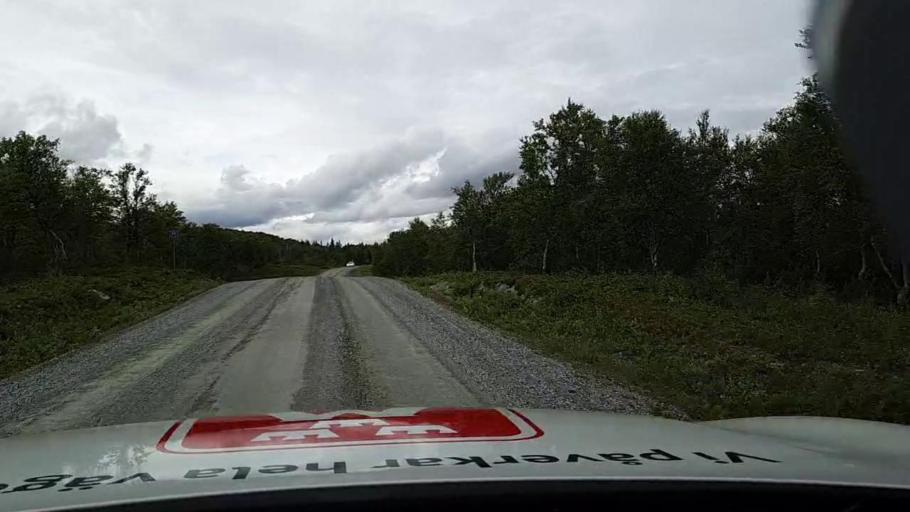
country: SE
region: Jaemtland
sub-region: Are Kommun
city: Are
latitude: 62.8888
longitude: 12.7183
